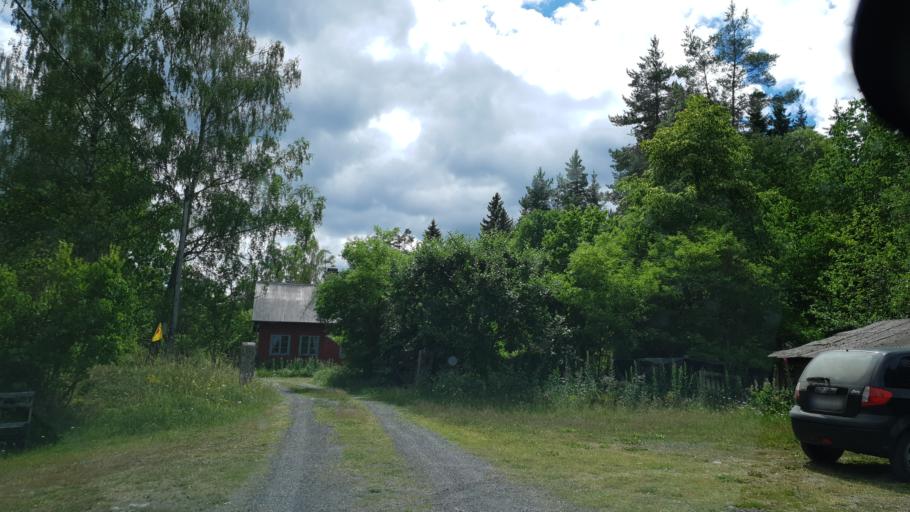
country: SE
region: Kalmar
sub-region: Hultsfreds Kommun
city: Virserum
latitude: 57.0925
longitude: 15.6380
